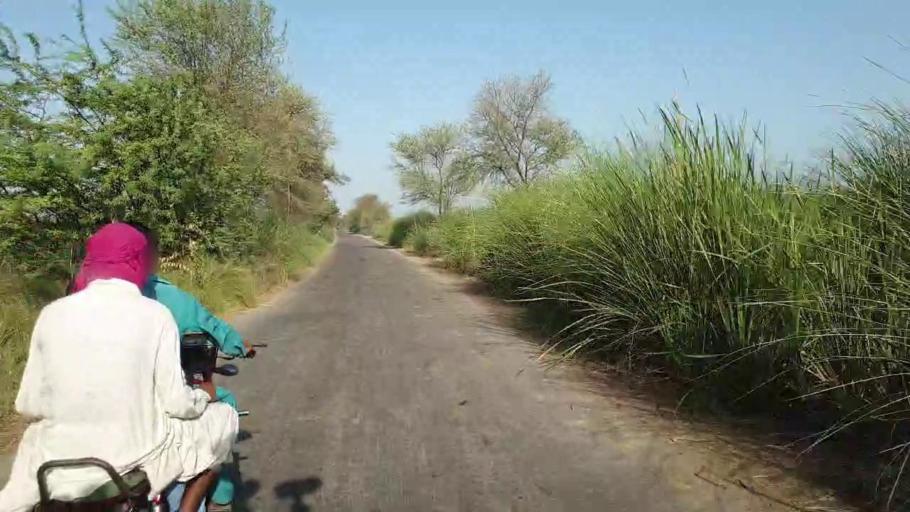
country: PK
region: Sindh
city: Nawabshah
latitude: 26.3738
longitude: 68.4683
